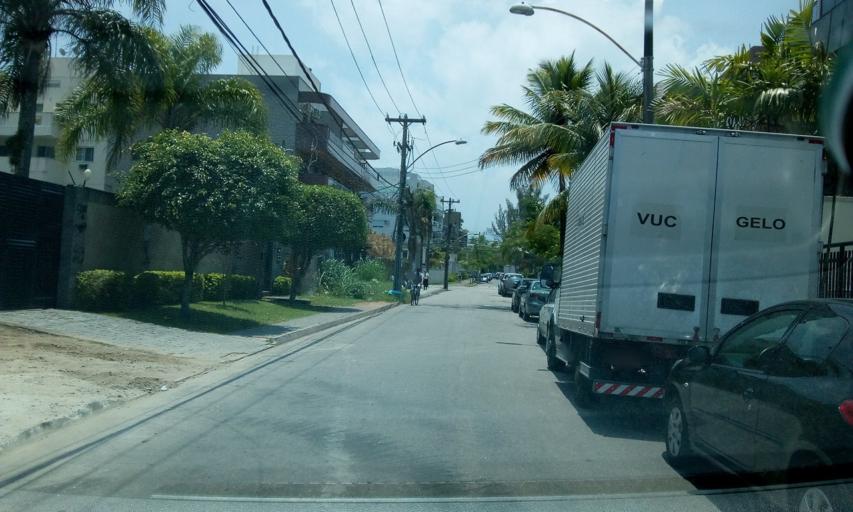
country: BR
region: Rio de Janeiro
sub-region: Nilopolis
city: Nilopolis
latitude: -23.0218
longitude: -43.4758
